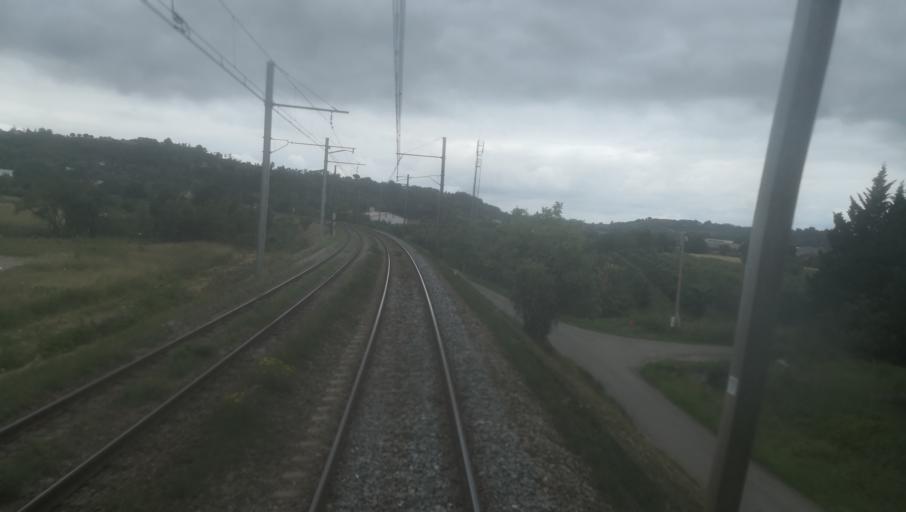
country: FR
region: Midi-Pyrenees
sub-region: Departement du Tarn-et-Garonne
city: Moissac
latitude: 44.0996
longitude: 1.1060
